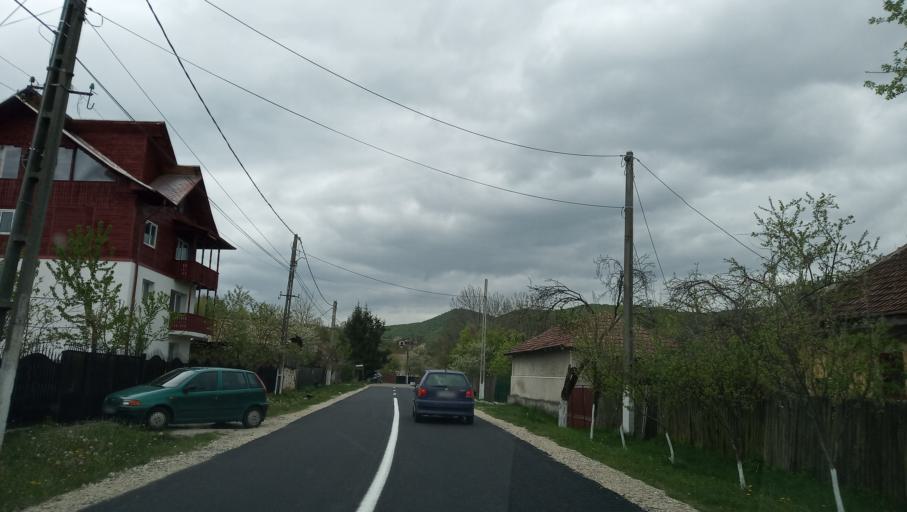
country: RO
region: Valcea
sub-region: Comuna Bujoreni
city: Bujoreni
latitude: 45.1508
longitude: 24.3924
